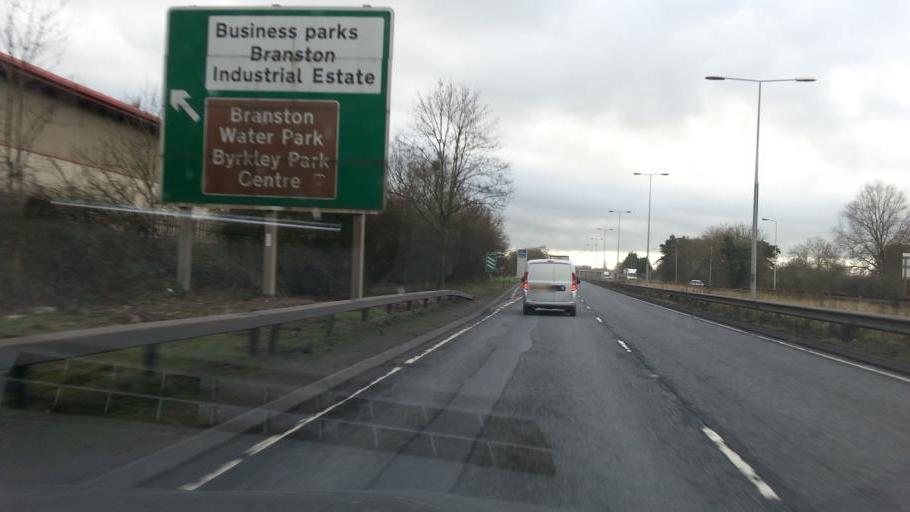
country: GB
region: England
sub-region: Staffordshire
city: Barton under Needwood
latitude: 52.7656
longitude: -1.6957
